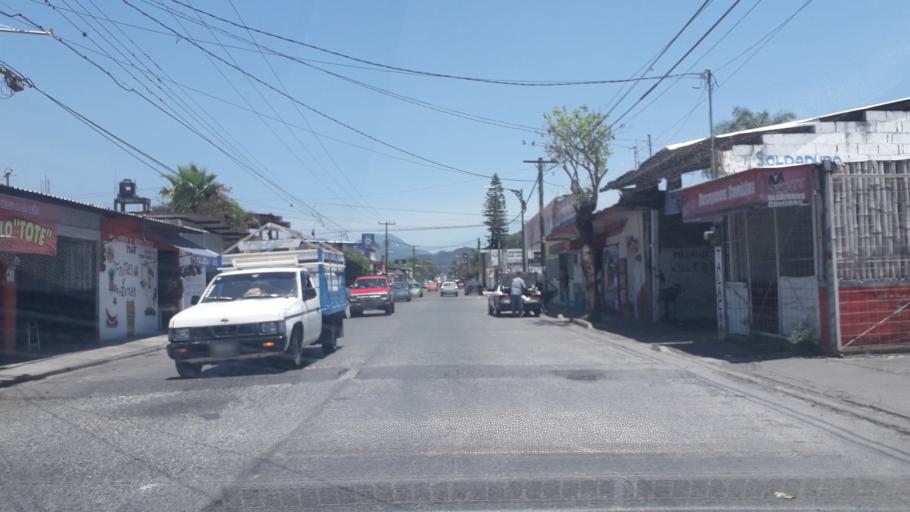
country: MX
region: Veracruz
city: Jalapilla
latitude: 18.8259
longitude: -97.0900
